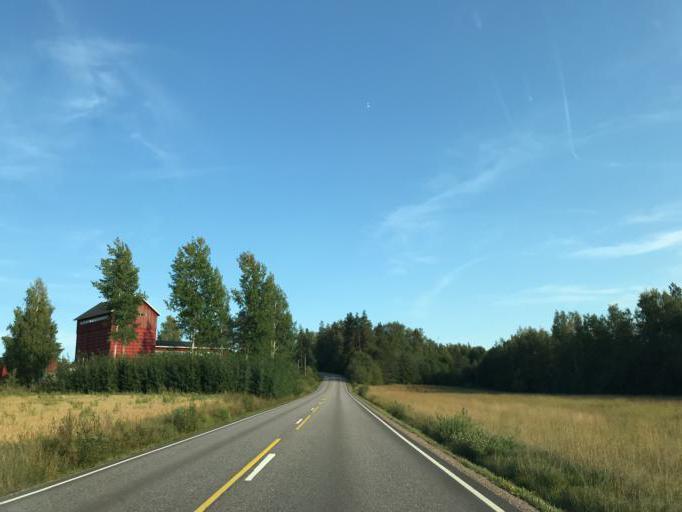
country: FI
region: Uusimaa
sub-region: Helsinki
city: Vihti
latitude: 60.4211
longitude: 24.3669
